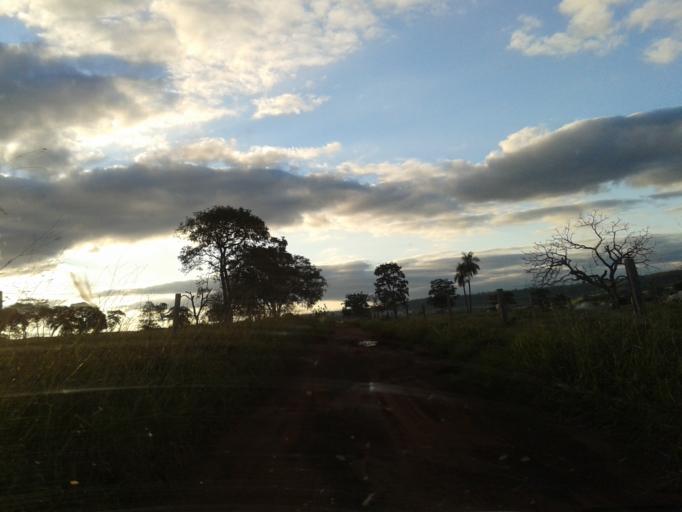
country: BR
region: Minas Gerais
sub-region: Campina Verde
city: Campina Verde
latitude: -19.5095
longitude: -49.6797
